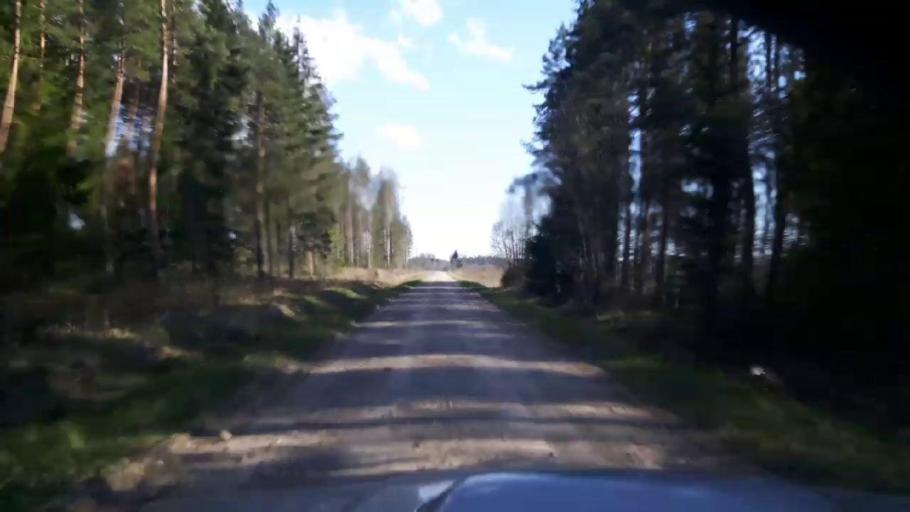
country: EE
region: Paernumaa
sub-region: Tootsi vald
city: Tootsi
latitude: 58.4203
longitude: 24.8518
